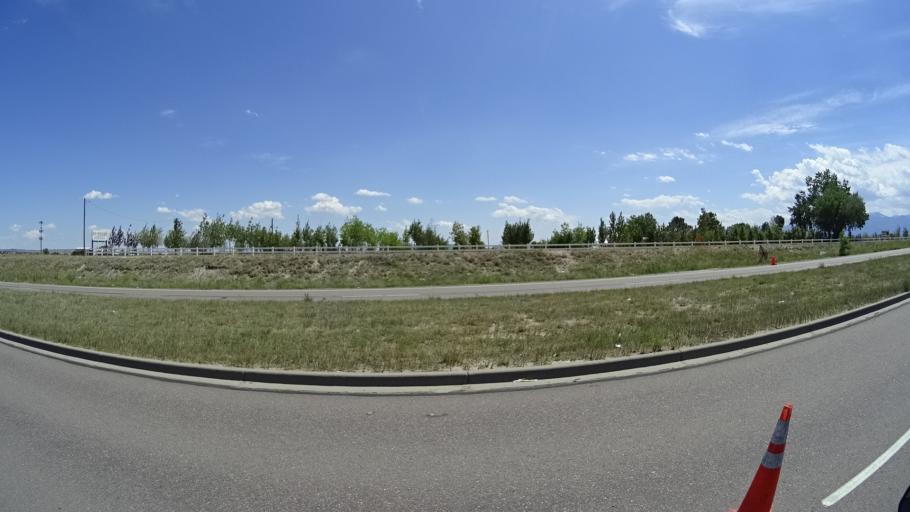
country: US
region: Colorado
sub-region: El Paso County
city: Black Forest
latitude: 38.9409
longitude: -104.7062
